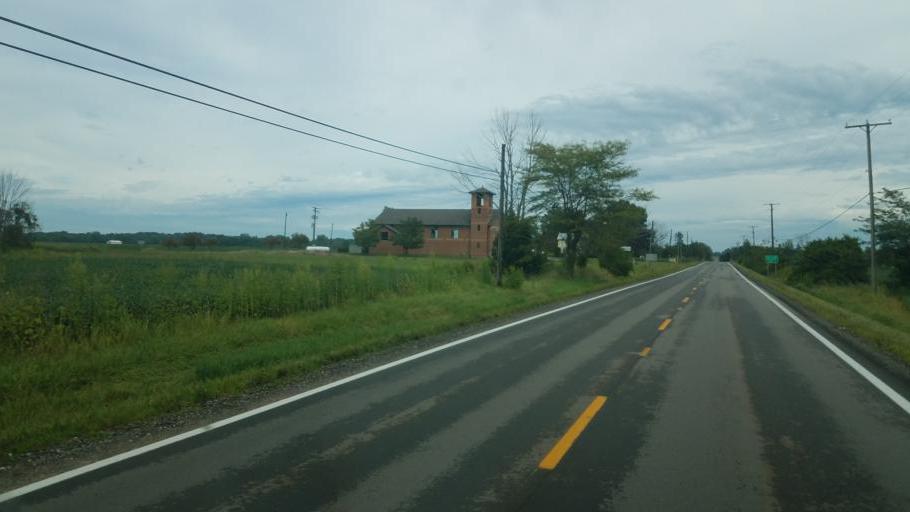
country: US
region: Ohio
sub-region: Morrow County
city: Mount Gilead
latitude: 40.5162
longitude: -82.8511
